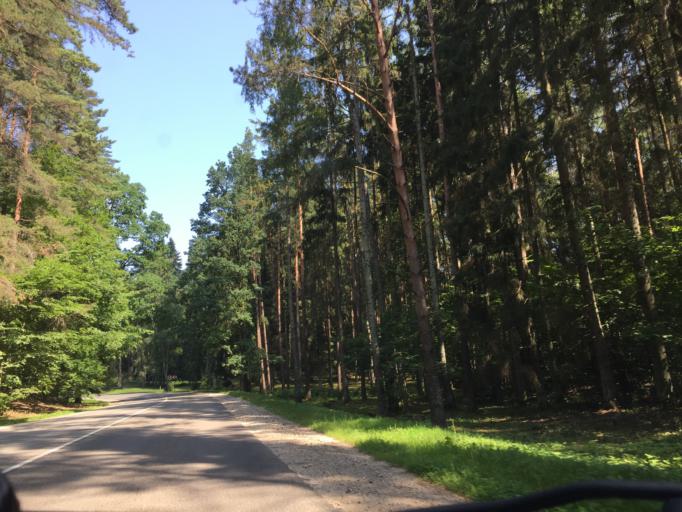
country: LV
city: Tervete
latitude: 56.4846
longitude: 23.3732
